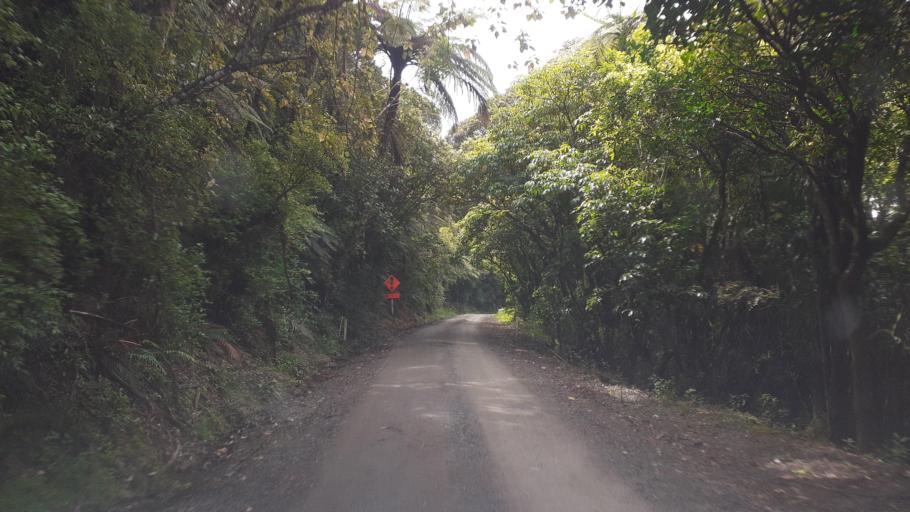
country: NZ
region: Northland
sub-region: Far North District
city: Waimate North
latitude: -35.5728
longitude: 173.5638
